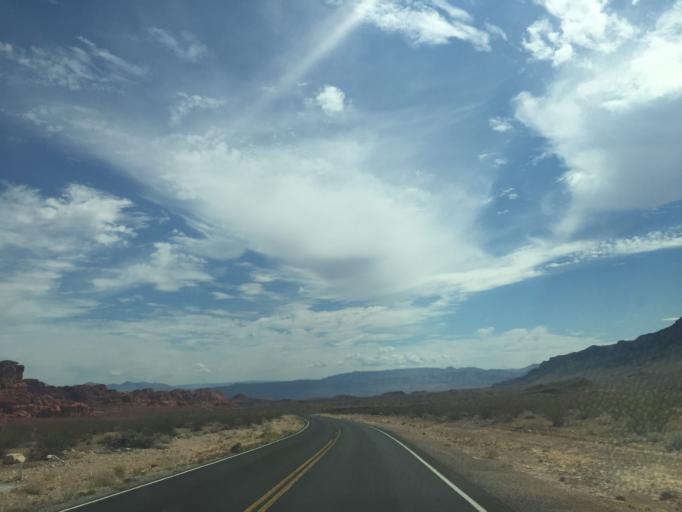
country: US
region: Nevada
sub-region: Clark County
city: Moapa Valley
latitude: 36.4256
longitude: -114.5372
